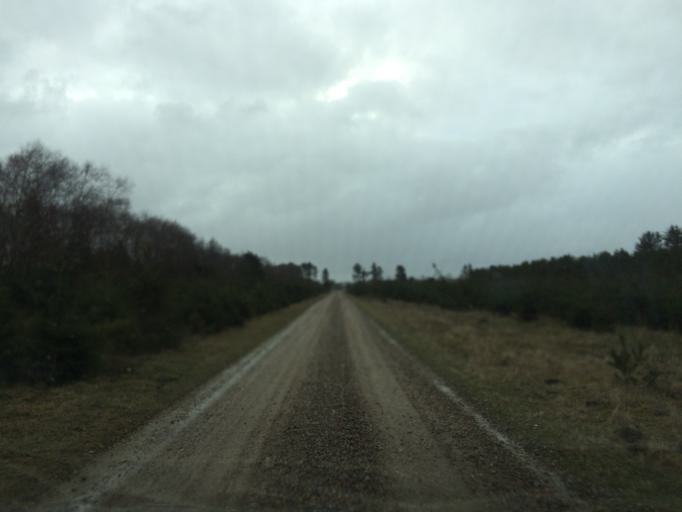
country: DK
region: Central Jutland
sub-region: Holstebro Kommune
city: Ulfborg
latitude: 56.2473
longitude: 8.4314
